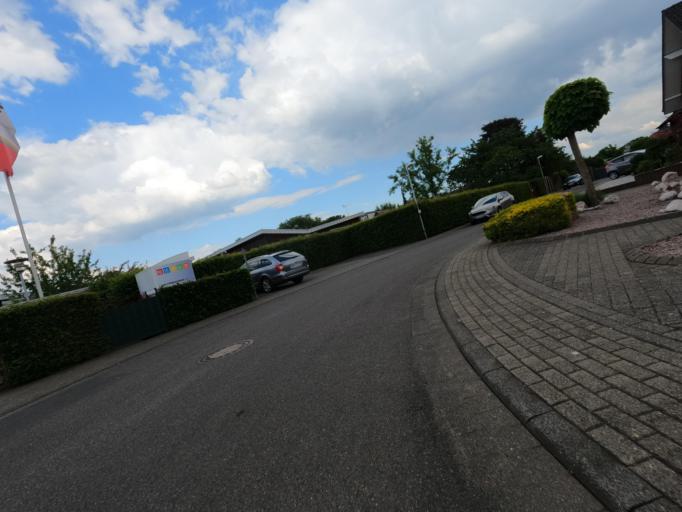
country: DE
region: North Rhine-Westphalia
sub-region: Regierungsbezirk Koln
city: Wassenberg
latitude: 51.0666
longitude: 6.1812
